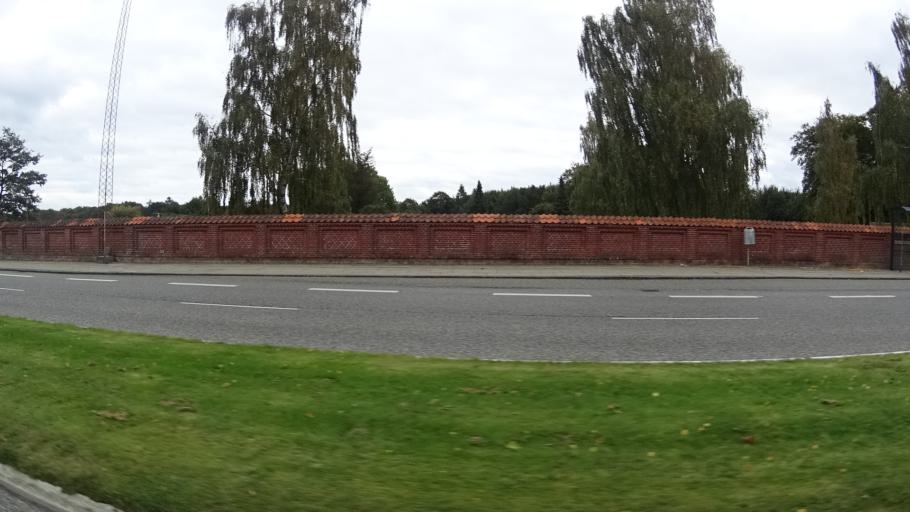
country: DK
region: South Denmark
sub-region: Vejle Kommune
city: Vejle
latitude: 55.6935
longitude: 9.5236
